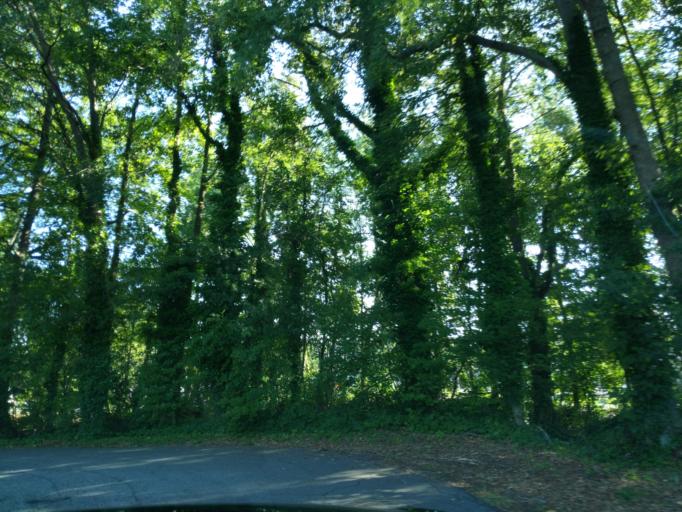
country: US
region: South Carolina
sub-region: Spartanburg County
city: Spartanburg
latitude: 34.9431
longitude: -81.9119
